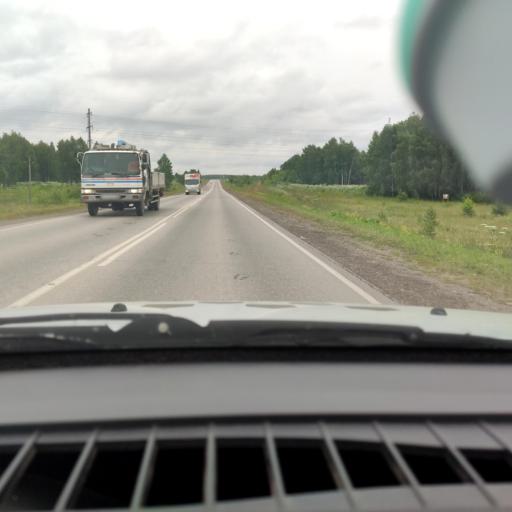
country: RU
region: Perm
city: Kungur
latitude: 57.4491
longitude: 56.9956
